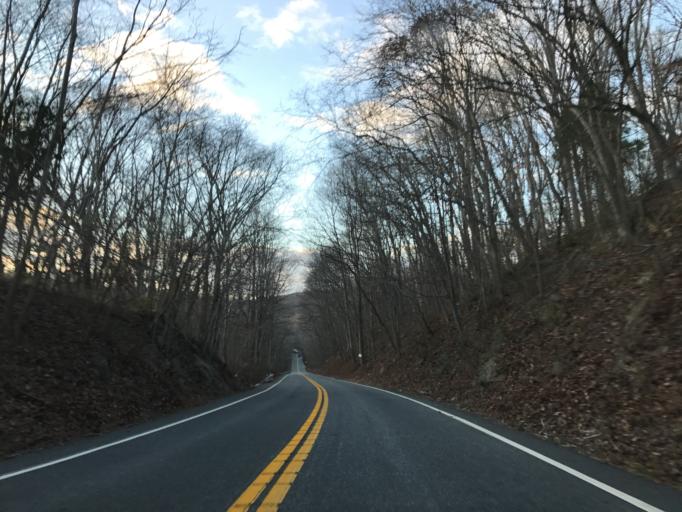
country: US
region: Pennsylvania
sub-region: York County
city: Susquehanna Trails
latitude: 39.6922
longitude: -76.2370
